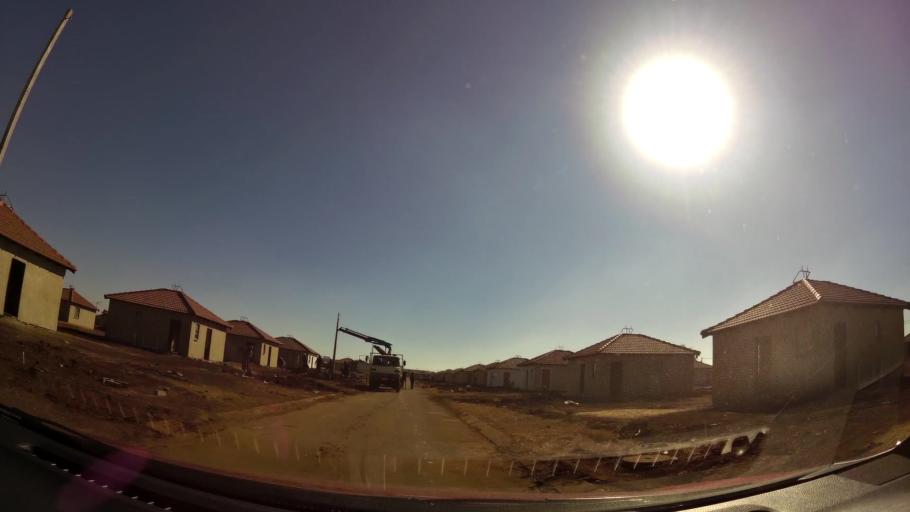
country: ZA
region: Gauteng
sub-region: City of Johannesburg Metropolitan Municipality
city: Soweto
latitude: -26.2399
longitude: 27.8038
